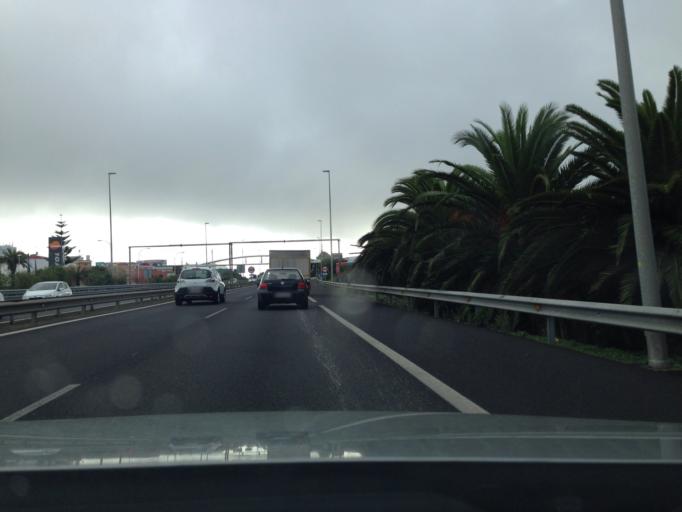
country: ES
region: Canary Islands
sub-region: Provincia de Santa Cruz de Tenerife
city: La Laguna
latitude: 28.4904
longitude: -16.3555
